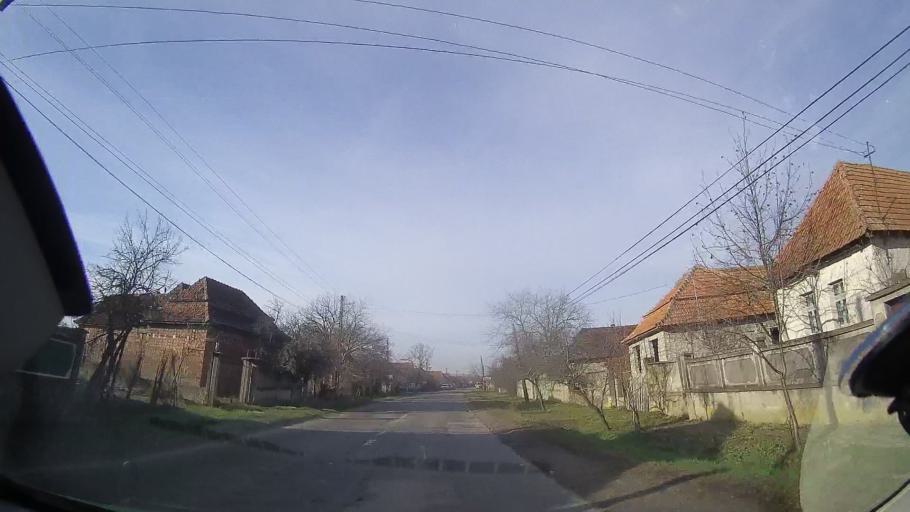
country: RO
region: Bihor
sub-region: Comuna Brusturi
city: Brusturi
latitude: 47.1499
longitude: 22.2514
